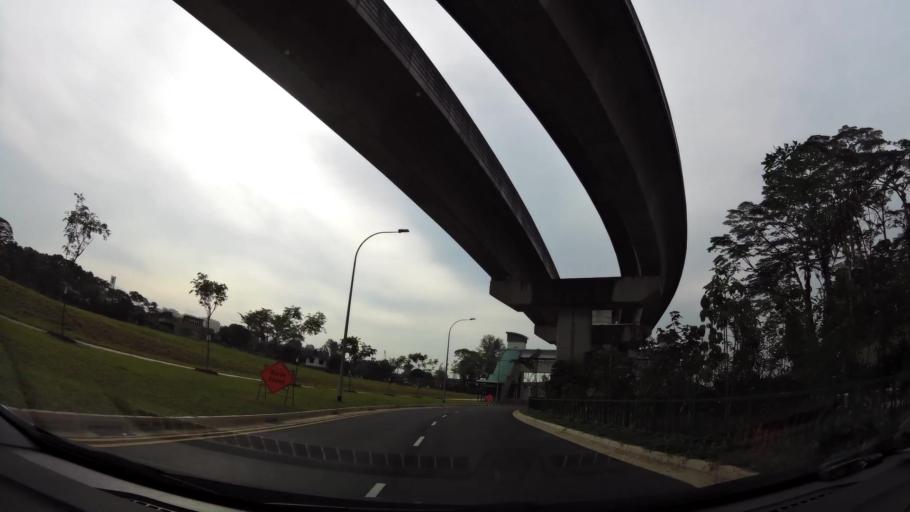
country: MY
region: Johor
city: Kampung Pasir Gudang Baru
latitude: 1.4166
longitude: 103.9072
